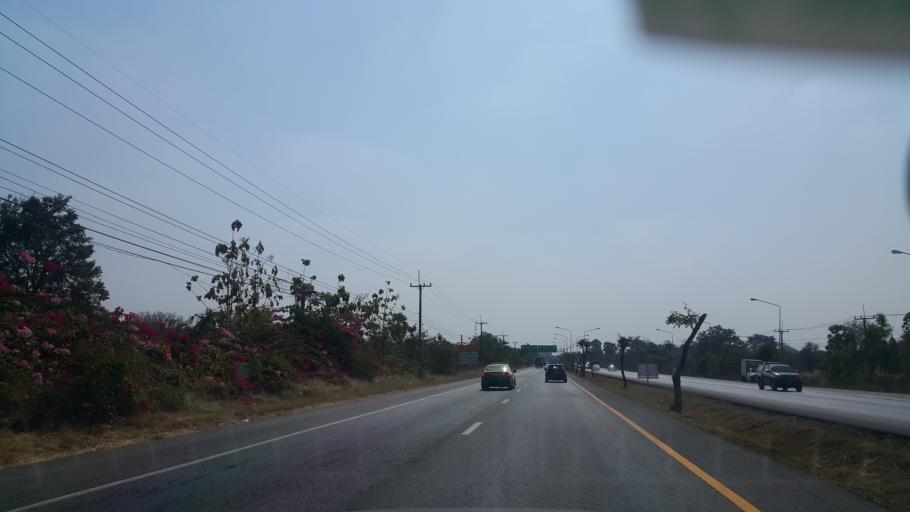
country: TH
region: Nakhon Ratchasima
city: Non Daeng
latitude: 15.3529
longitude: 102.4482
